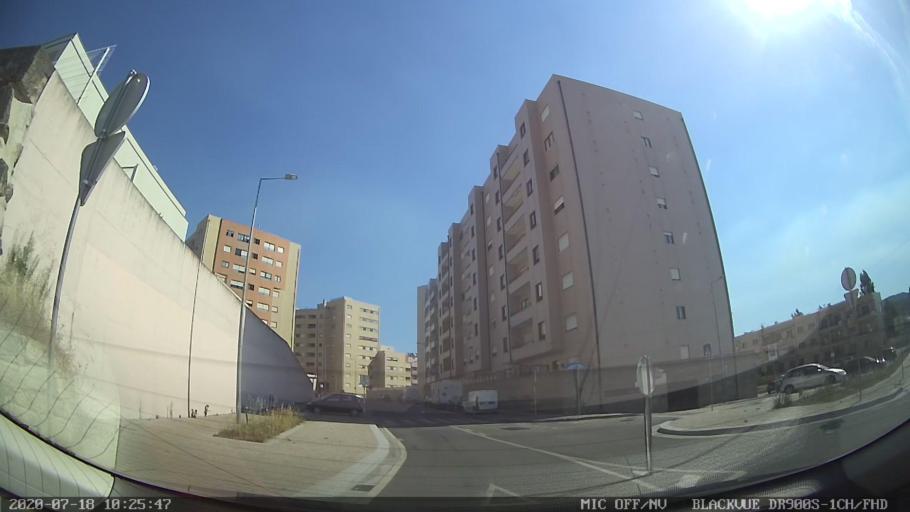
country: PT
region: Porto
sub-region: Gondomar
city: Rio Tinto
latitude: 41.1742
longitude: -8.5434
